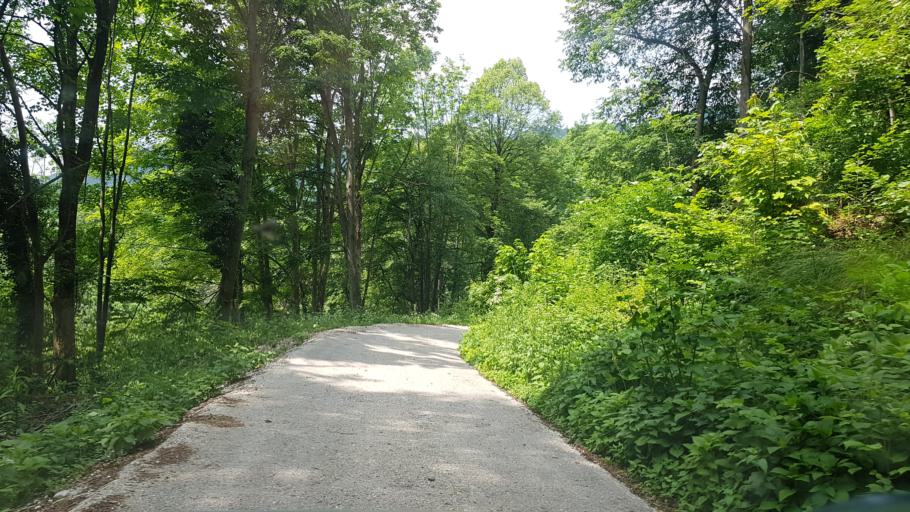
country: IT
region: Friuli Venezia Giulia
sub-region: Provincia di Udine
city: Torreano
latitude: 46.1779
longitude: 13.4335
